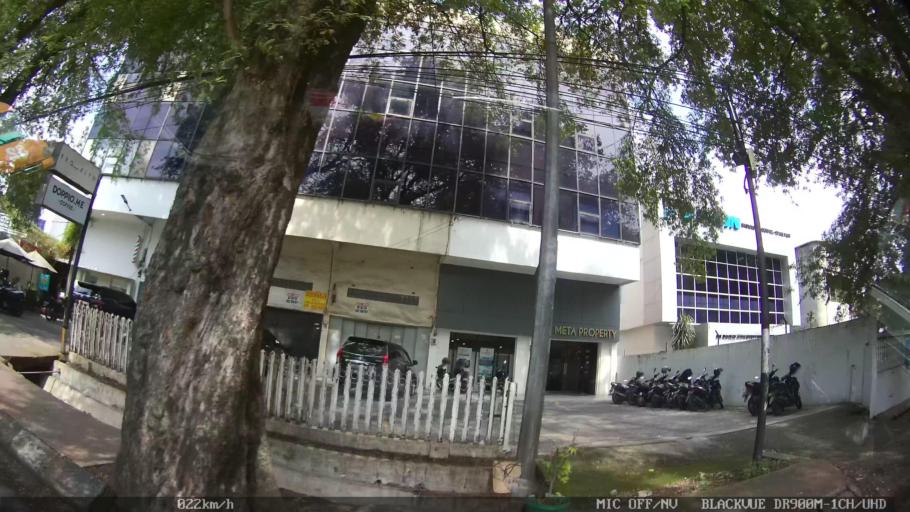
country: ID
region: North Sumatra
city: Medan
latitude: 3.5963
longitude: 98.6690
